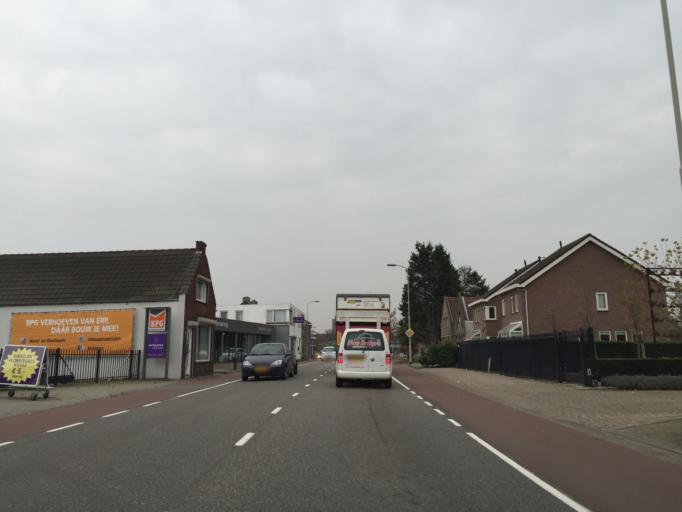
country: NL
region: North Brabant
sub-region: Roosendaal
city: Roosendaal
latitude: 51.5483
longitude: 4.4736
